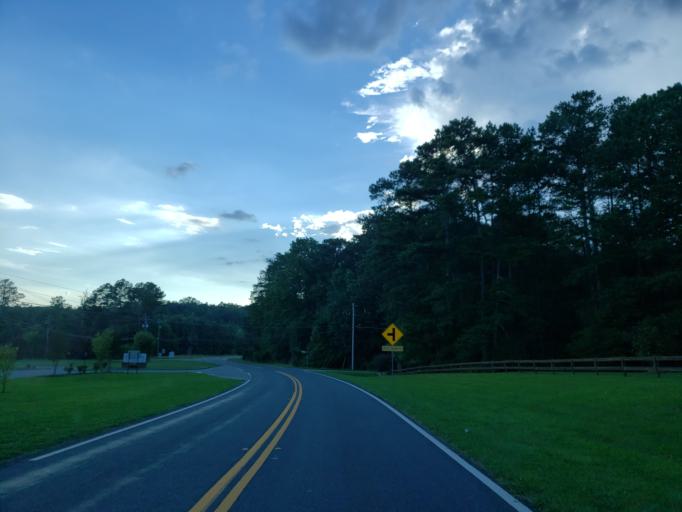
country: US
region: Georgia
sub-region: Bartow County
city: Cartersville
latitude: 34.2072
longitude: -84.7526
